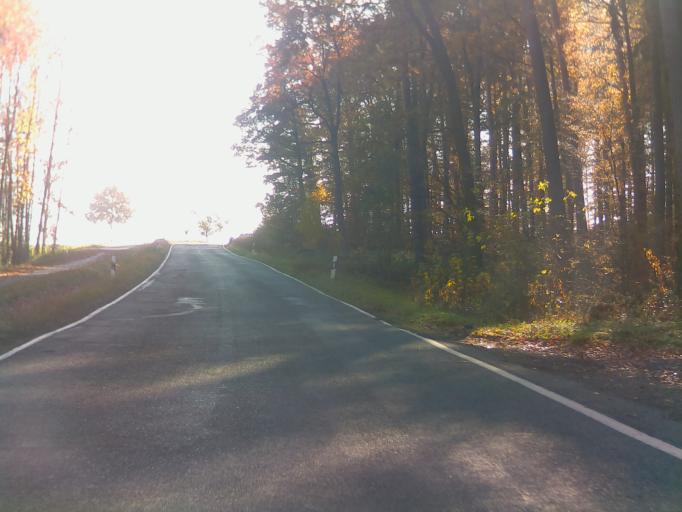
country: DE
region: Bavaria
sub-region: Upper Franconia
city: Burgwindheim
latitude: 49.8804
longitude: 10.5582
